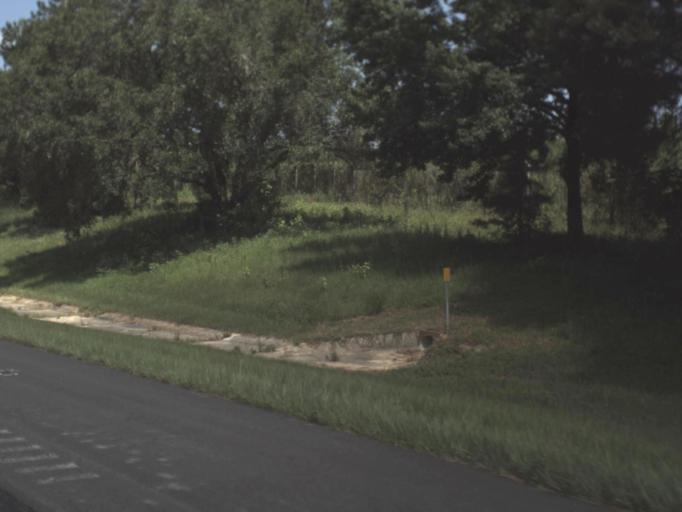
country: US
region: Florida
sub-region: Madison County
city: Madison
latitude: 30.4357
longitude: -83.4943
